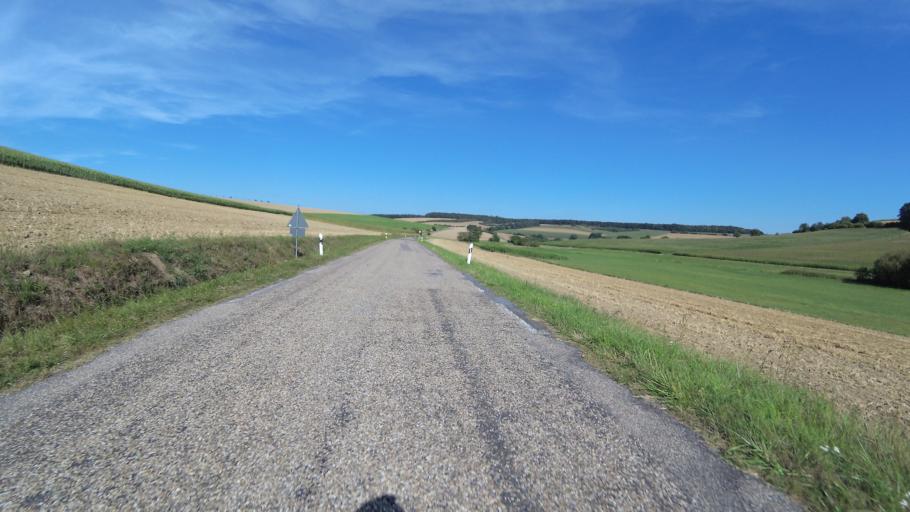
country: DE
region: Rheinland-Pfalz
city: Althornbach
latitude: 49.1847
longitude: 7.3063
